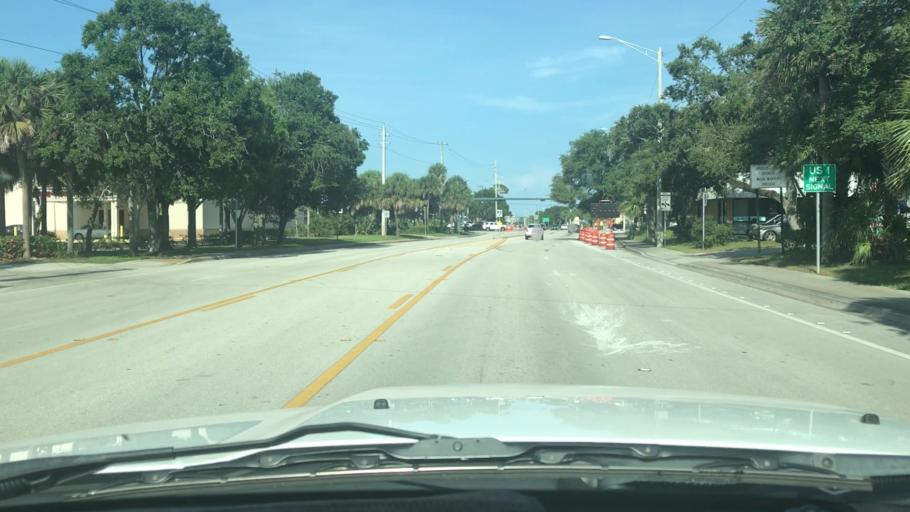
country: US
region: Florida
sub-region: Indian River County
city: Vero Beach
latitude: 27.6326
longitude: -80.3910
